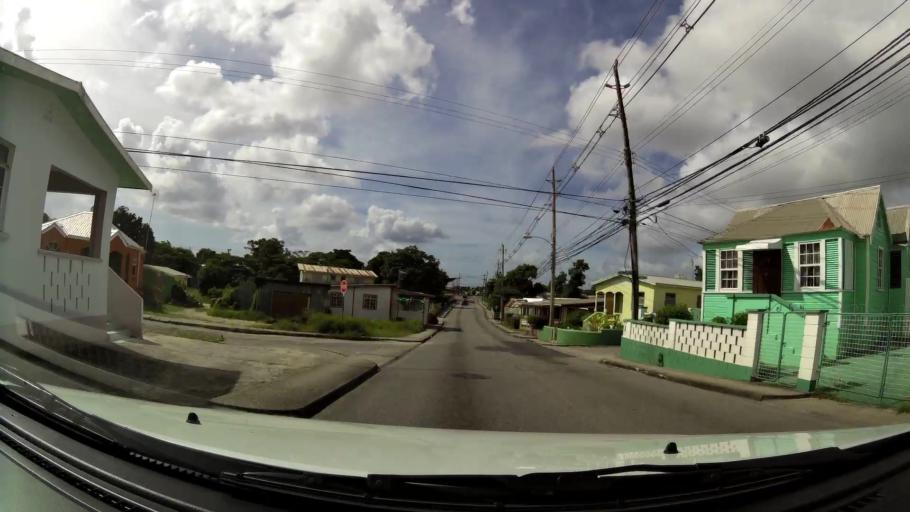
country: BB
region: Saint Michael
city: Bridgetown
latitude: 13.1064
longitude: -59.6037
